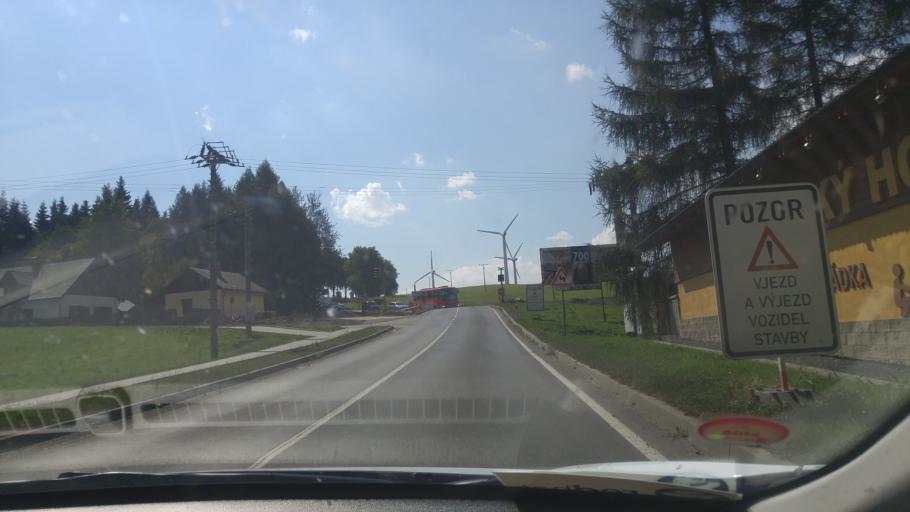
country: CZ
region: Olomoucky
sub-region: Okres Sumperk
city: Stare Mesto
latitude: 50.1849
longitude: 17.0510
